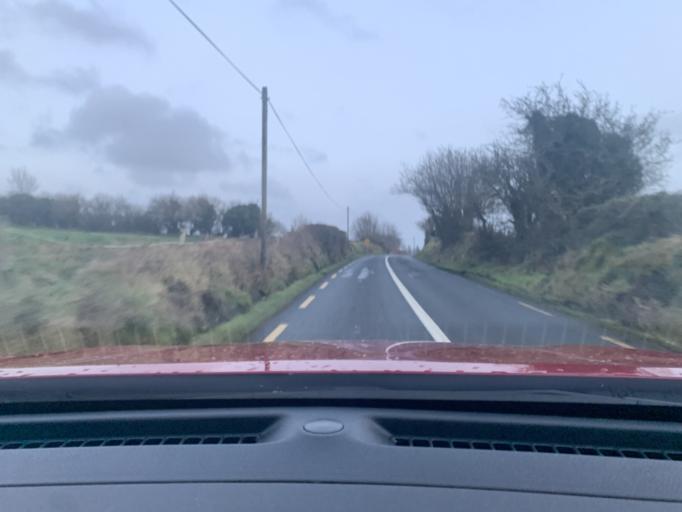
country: IE
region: Connaught
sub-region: Sligo
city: Ballymote
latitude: 54.0346
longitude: -8.4200
